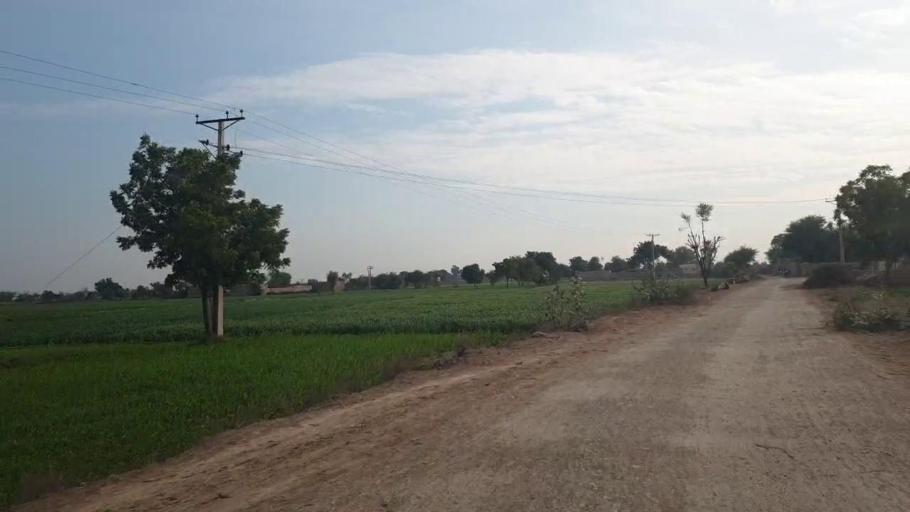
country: PK
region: Sindh
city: Shahpur Chakar
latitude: 26.0478
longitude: 68.5769
